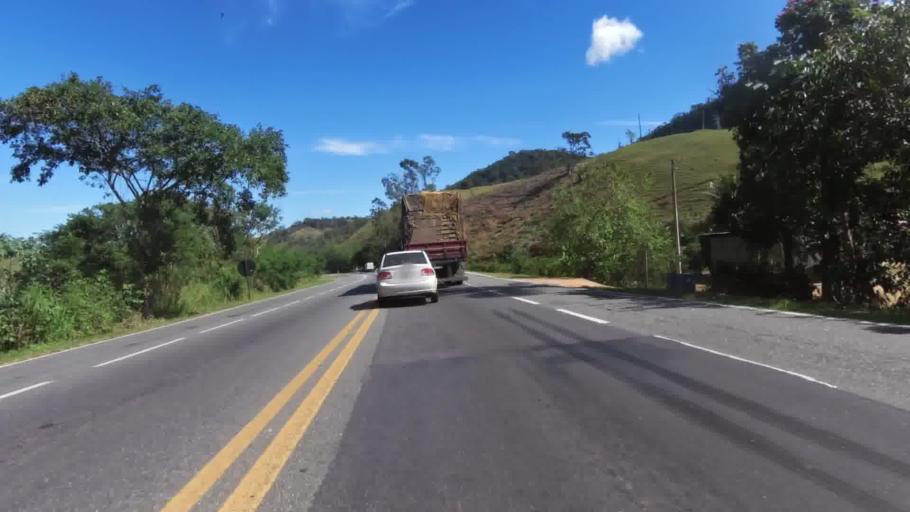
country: BR
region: Espirito Santo
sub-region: Rio Novo Do Sul
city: Rio Novo do Sul
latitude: -20.8668
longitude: -40.9064
